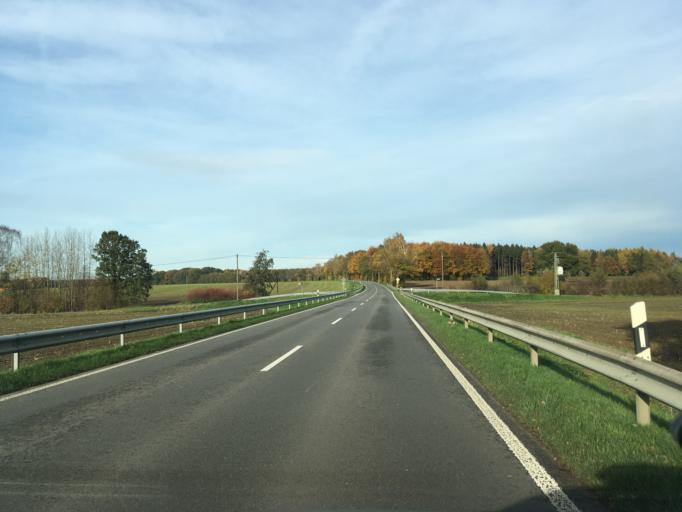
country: DE
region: North Rhine-Westphalia
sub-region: Regierungsbezirk Munster
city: Heiden
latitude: 51.8373
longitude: 6.9334
